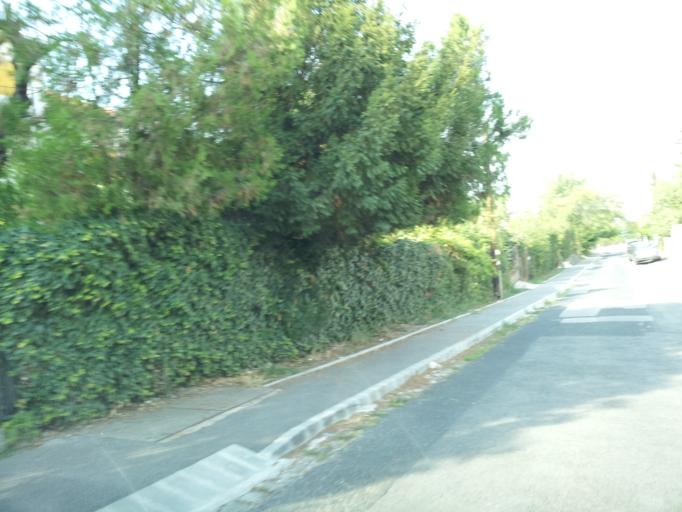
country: HU
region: Budapest
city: Budapest II. keruelet
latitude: 47.5238
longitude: 19.0297
